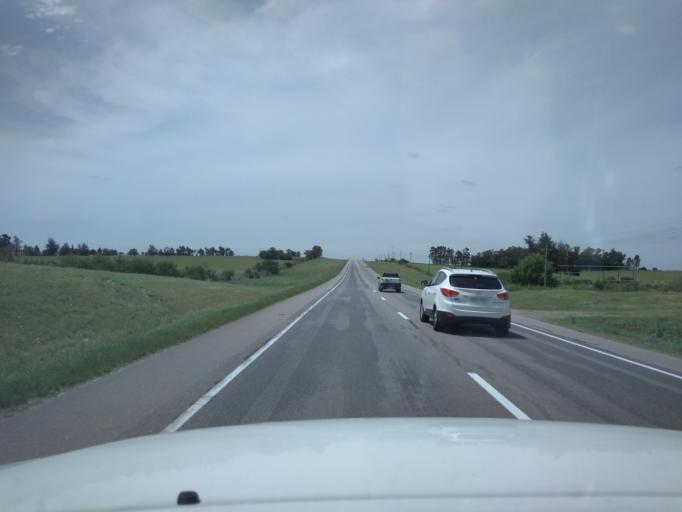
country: UY
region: Florida
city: Florida
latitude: -34.2179
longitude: -56.2081
